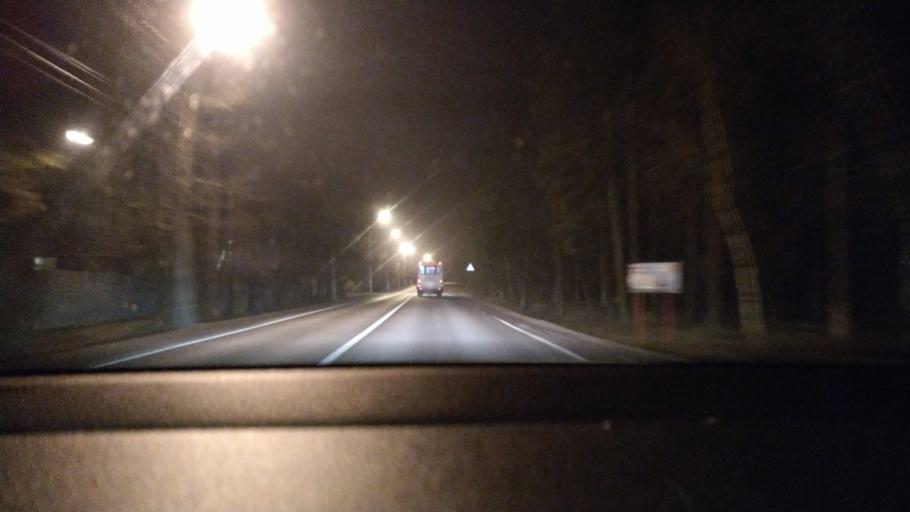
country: RU
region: Moskovskaya
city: Selyatino
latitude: 55.4781
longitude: 36.9246
